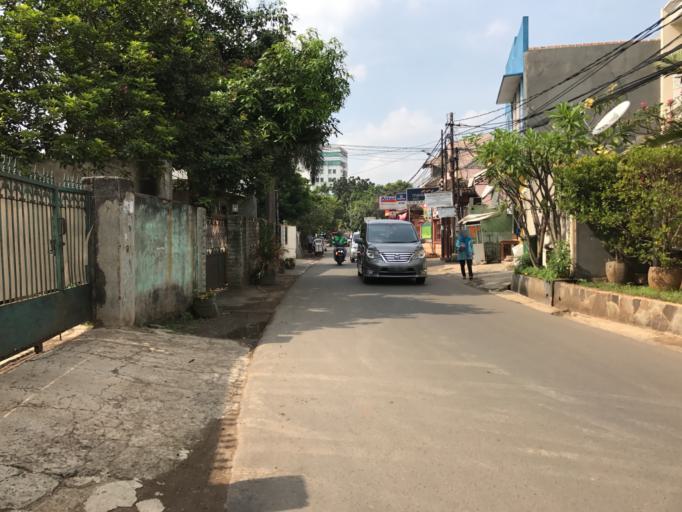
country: ID
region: Jakarta Raya
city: Jakarta
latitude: -6.2891
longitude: 106.8126
